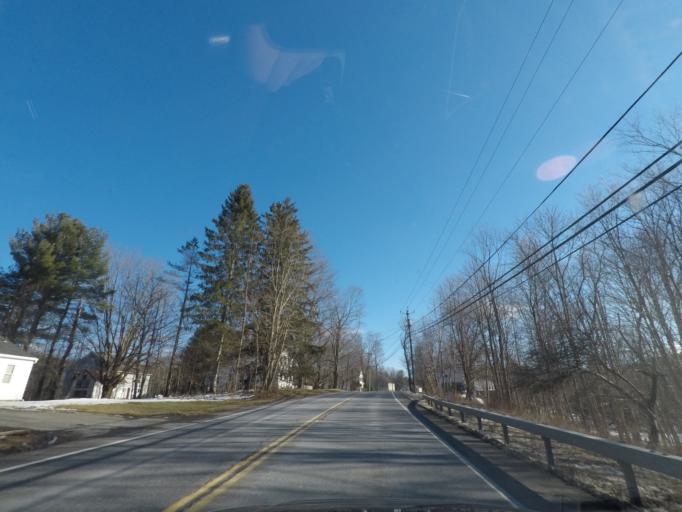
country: US
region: New York
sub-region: Columbia County
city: Chatham
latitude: 42.3274
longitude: -73.5491
